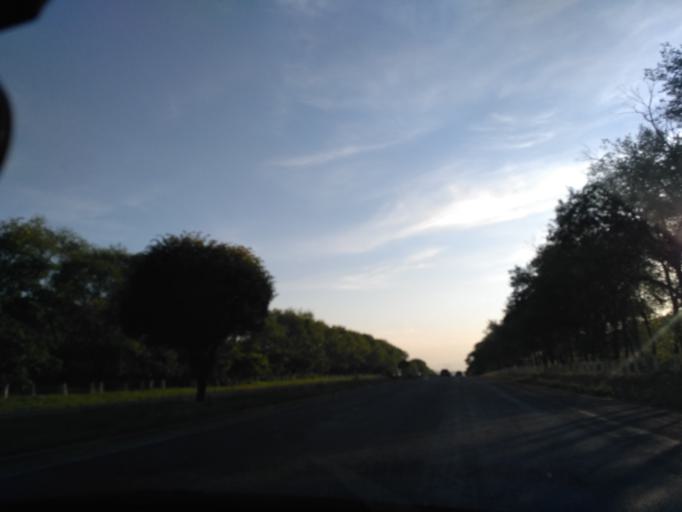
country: KZ
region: Almaty Oblysy
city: Burunday
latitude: 43.2219
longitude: 76.5598
